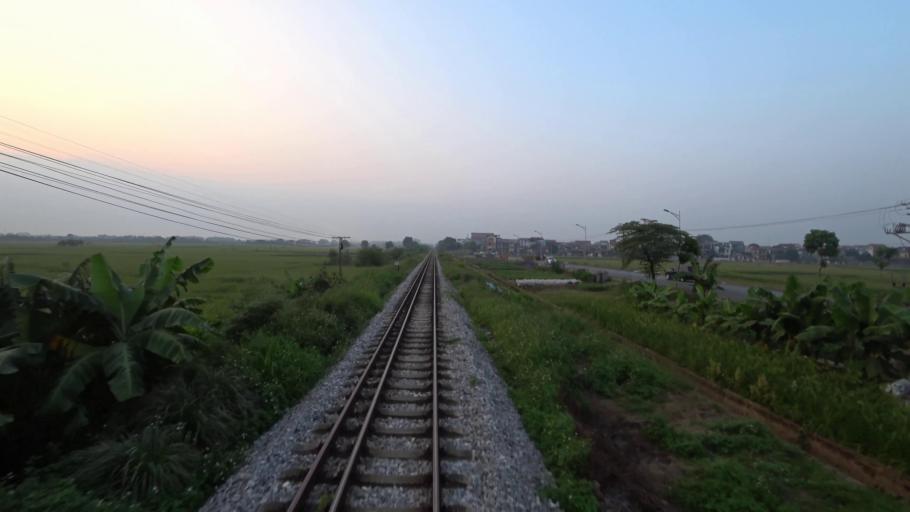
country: VN
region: Ha Noi
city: Dong Anh
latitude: 21.1272
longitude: 105.8794
